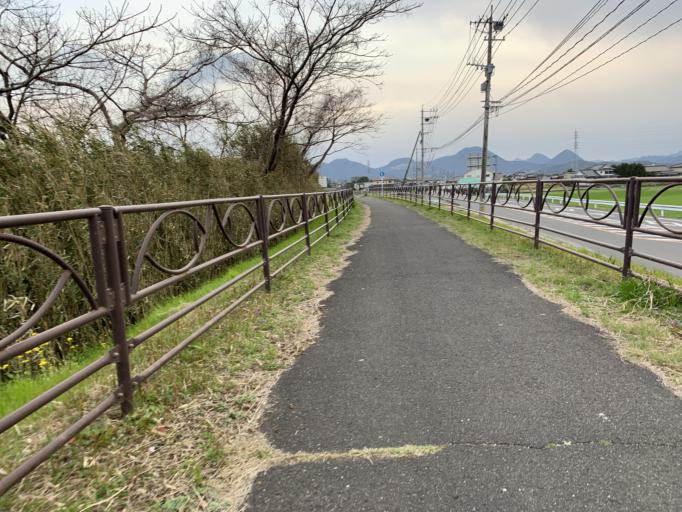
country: JP
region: Oita
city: Bungo-Takada-shi
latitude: 33.5413
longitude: 131.3542
